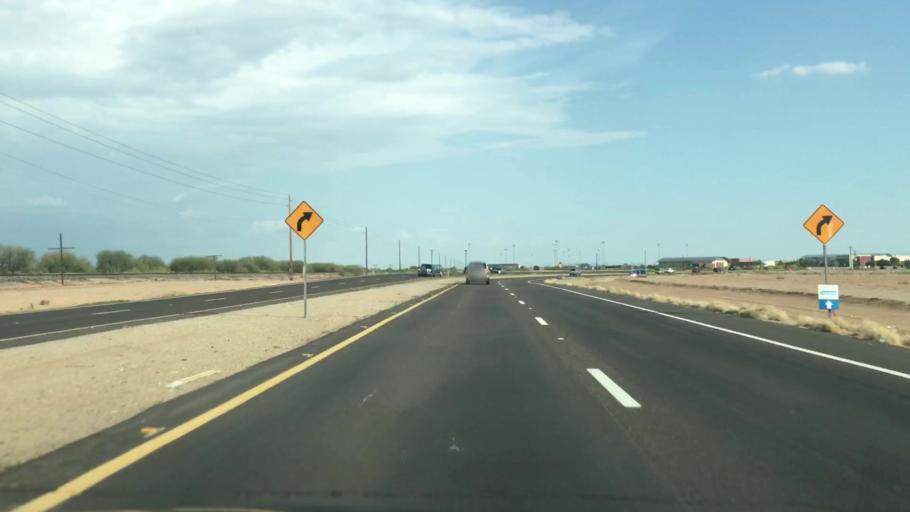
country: US
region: Arizona
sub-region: Pinal County
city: San Tan Valley
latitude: 33.1810
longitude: -111.5473
